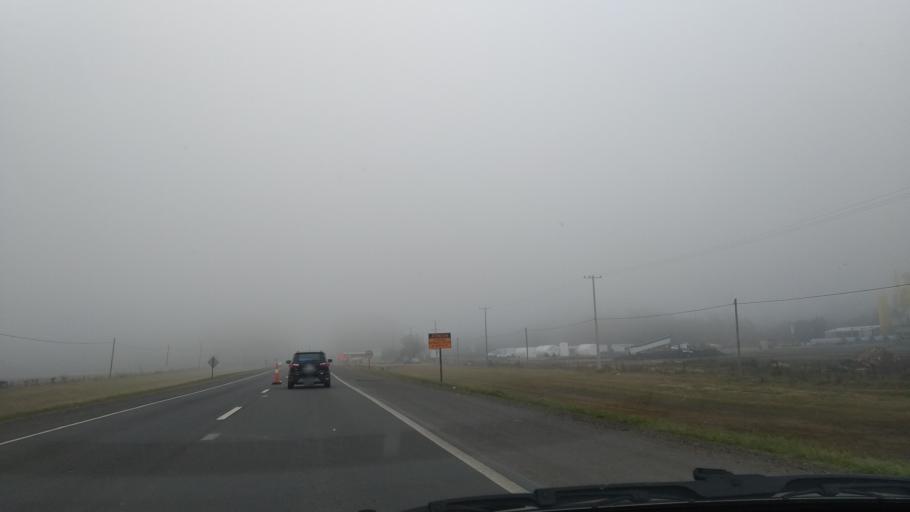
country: AR
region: Buenos Aires
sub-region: Partido de Azul
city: Azul
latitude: -36.8185
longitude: -59.8719
